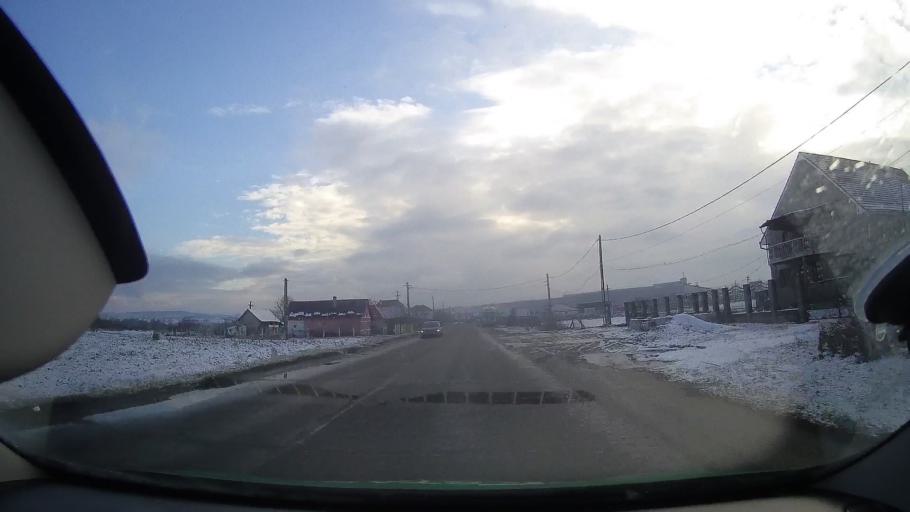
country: RO
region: Mures
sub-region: Comuna Iernut
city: Iernut
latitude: 46.4397
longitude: 24.2524
